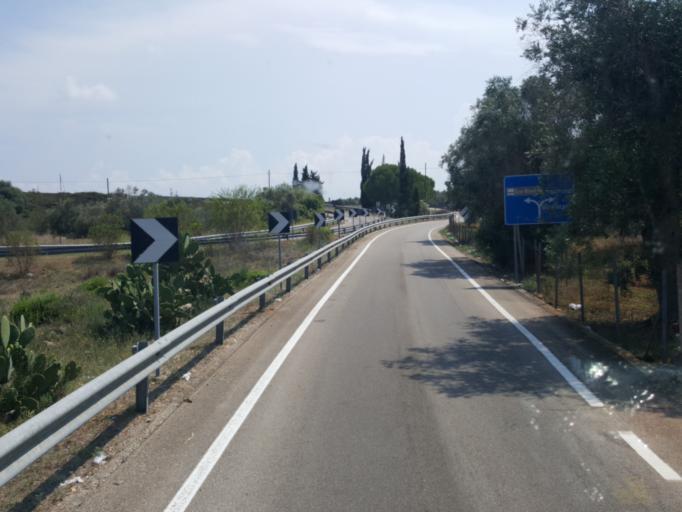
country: IT
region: Apulia
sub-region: Provincia di Lecce
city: Trepuzzi
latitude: 40.4408
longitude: 18.0771
